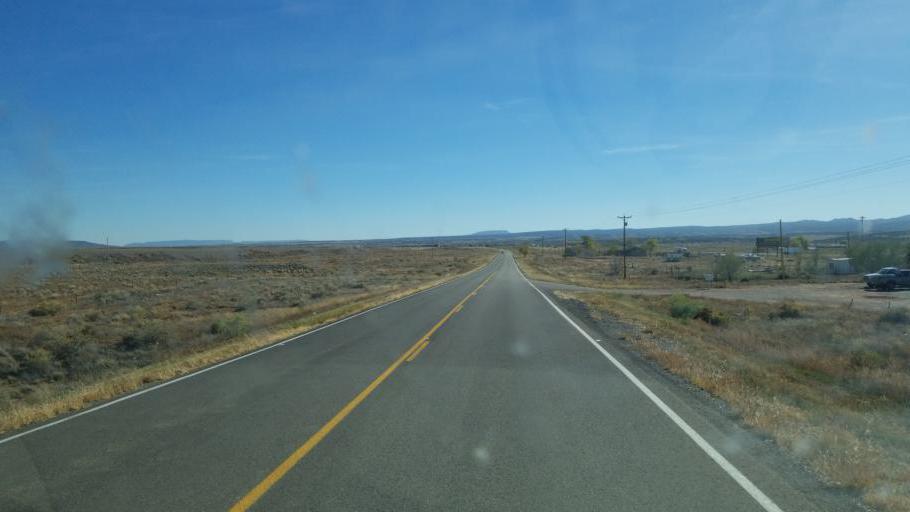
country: US
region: New Mexico
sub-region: Cibola County
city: Milan
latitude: 35.2975
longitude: -107.9871
